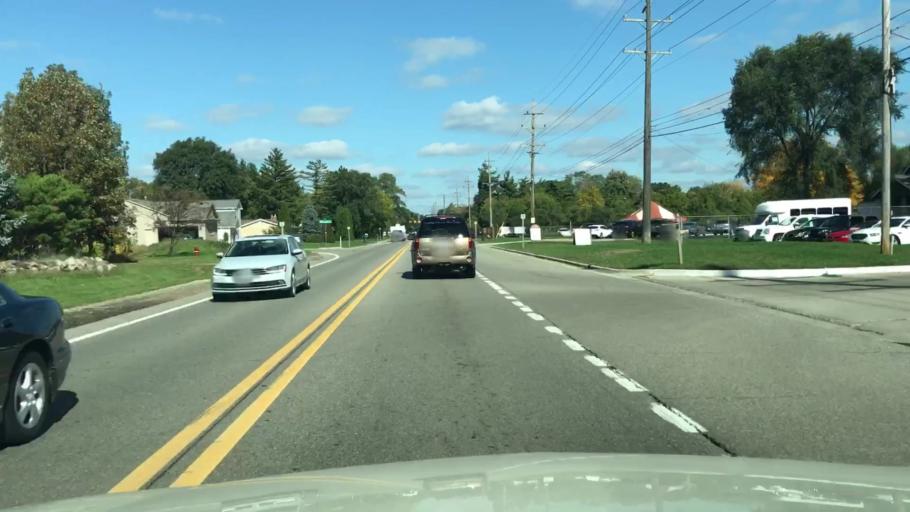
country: US
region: Michigan
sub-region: Macomb County
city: Utica
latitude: 42.6346
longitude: -83.0919
